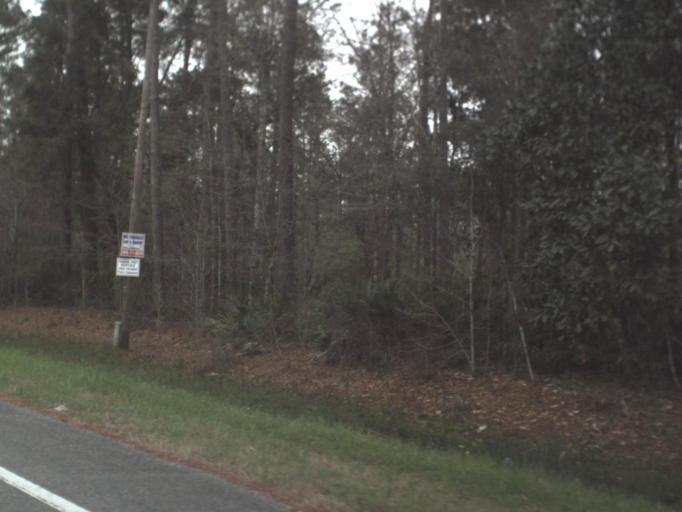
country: US
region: Florida
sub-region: Leon County
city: Woodville
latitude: 30.1989
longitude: -84.1731
